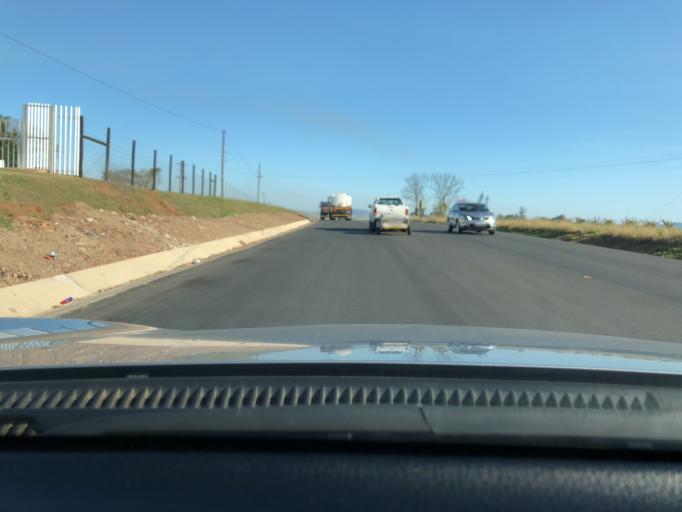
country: ZA
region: KwaZulu-Natal
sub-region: uMgungundlovu District Municipality
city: Camperdown
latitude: -29.7482
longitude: 30.5060
